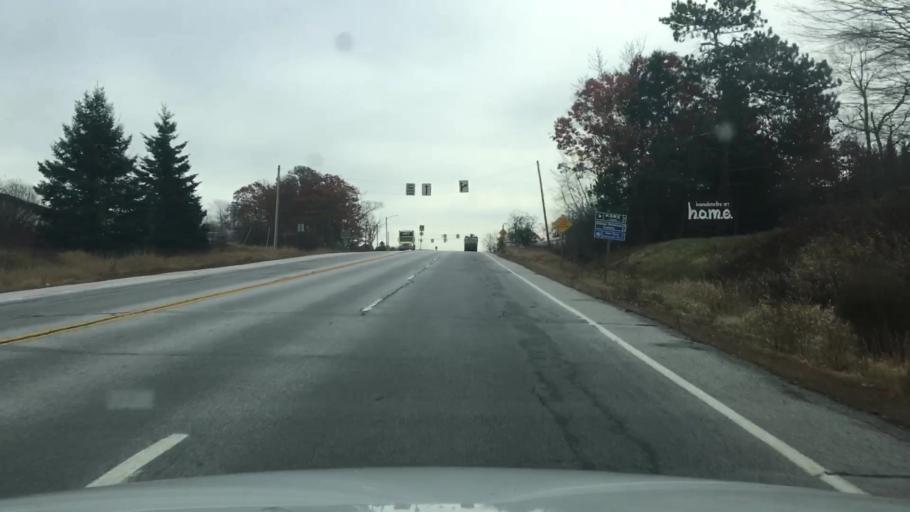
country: US
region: Maine
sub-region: Hancock County
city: Orland
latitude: 44.5752
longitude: -68.7338
